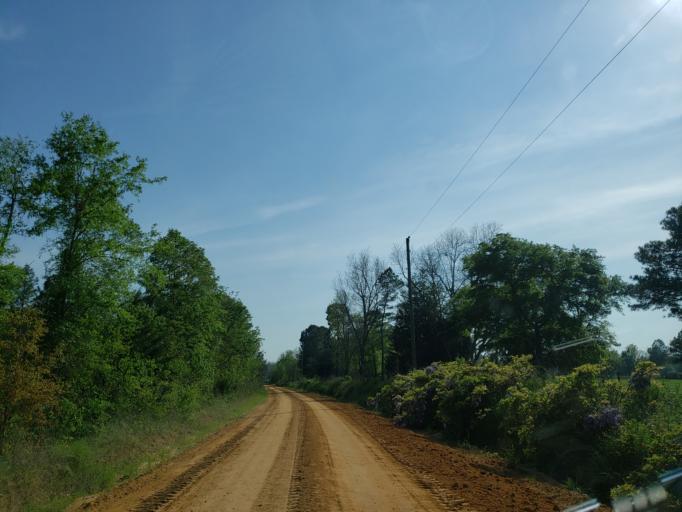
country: US
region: Georgia
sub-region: Dooly County
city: Vienna
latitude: 32.1011
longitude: -83.7856
